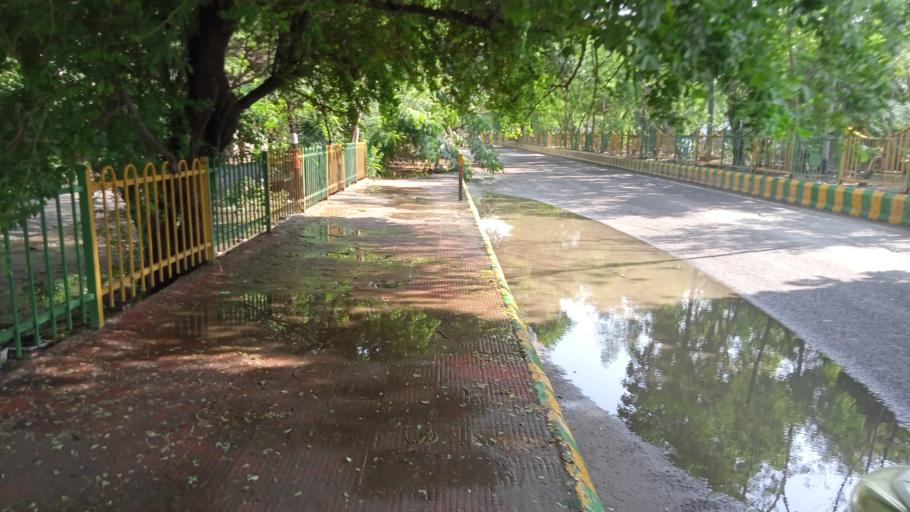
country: IN
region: Uttar Pradesh
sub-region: Ghaziabad
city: Ghaziabad
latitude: 28.6654
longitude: 77.3717
